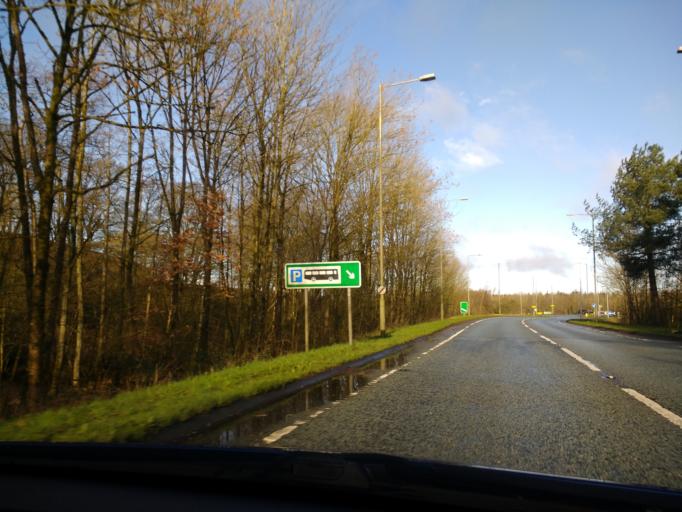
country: GB
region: England
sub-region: Cumbria
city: Cockermouth
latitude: 54.6652
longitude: -3.3927
